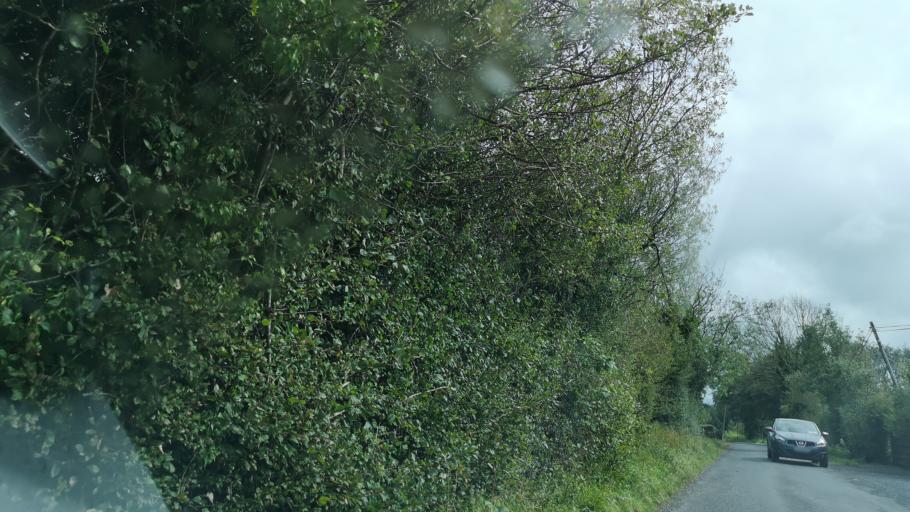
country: IE
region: Connaught
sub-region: County Galway
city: Loughrea
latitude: 53.3039
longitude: -8.6058
